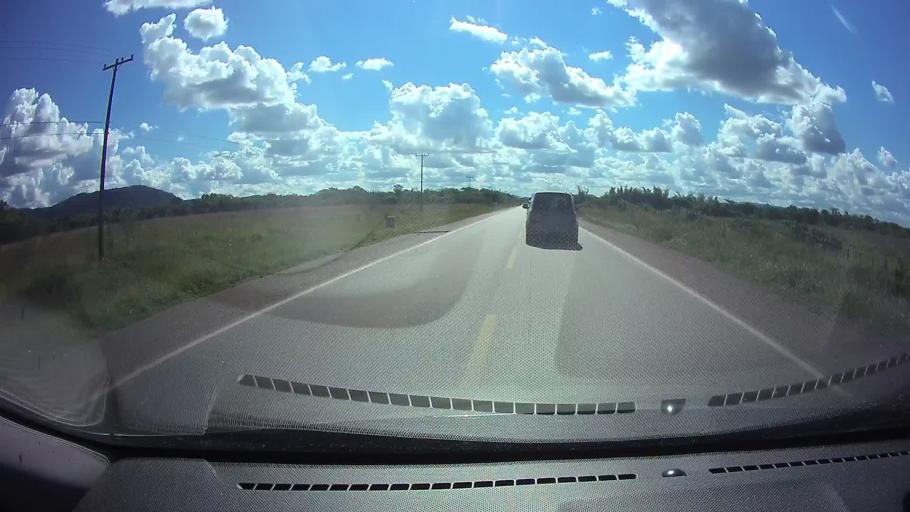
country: PY
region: Paraguari
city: La Colmena
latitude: -25.7532
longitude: -56.7775
